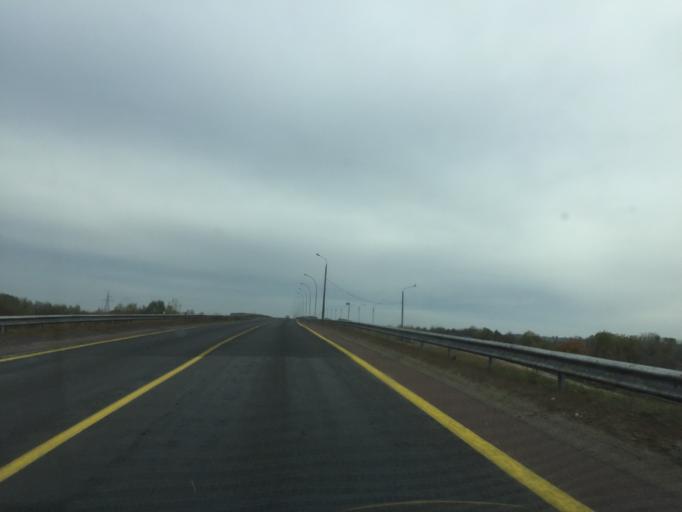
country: BY
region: Gomel
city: Horad Rechytsa
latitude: 52.3253
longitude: 30.5307
